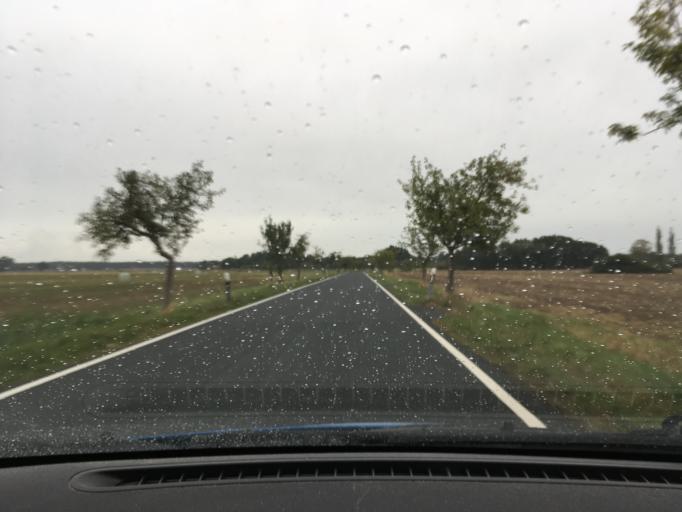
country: DE
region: Lower Saxony
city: Hitzacker
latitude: 53.1856
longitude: 11.0343
